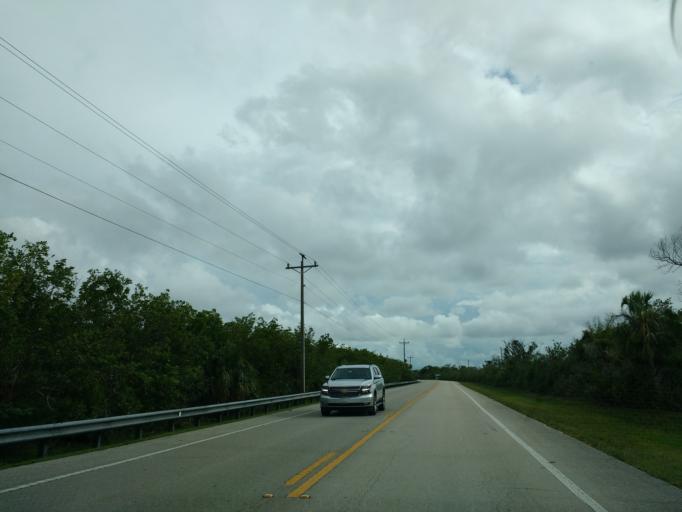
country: US
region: Florida
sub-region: Collier County
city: Marco
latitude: 25.8900
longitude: -81.3761
